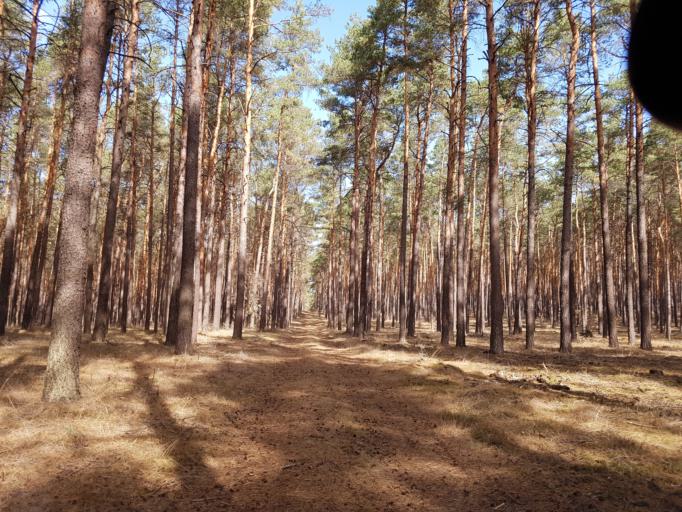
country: DE
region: Brandenburg
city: Sonnewalde
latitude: 51.7537
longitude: 13.6629
